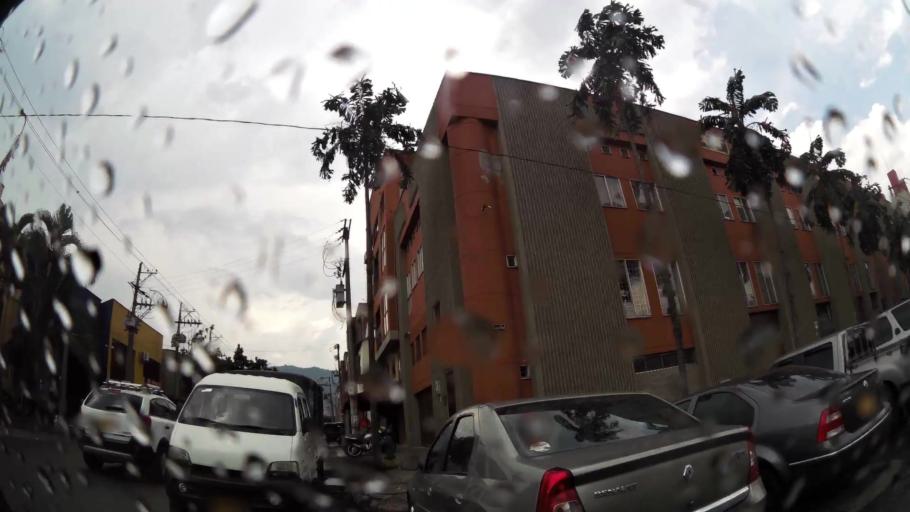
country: CO
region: Antioquia
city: Envigado
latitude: 6.1830
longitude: -75.5919
